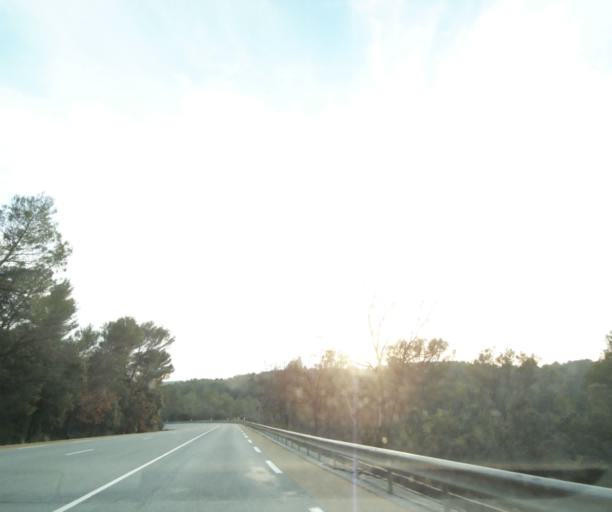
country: FR
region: Provence-Alpes-Cote d'Azur
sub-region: Departement du Var
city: Trans-en-Provence
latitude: 43.5057
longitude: 6.5102
